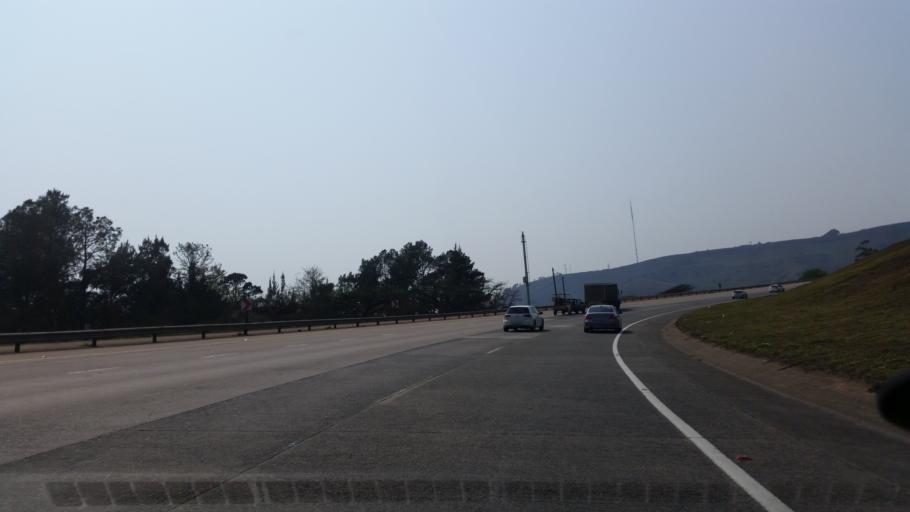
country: ZA
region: KwaZulu-Natal
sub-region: eThekwini Metropolitan Municipality
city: Mpumalanga
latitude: -29.7711
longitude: 30.6901
